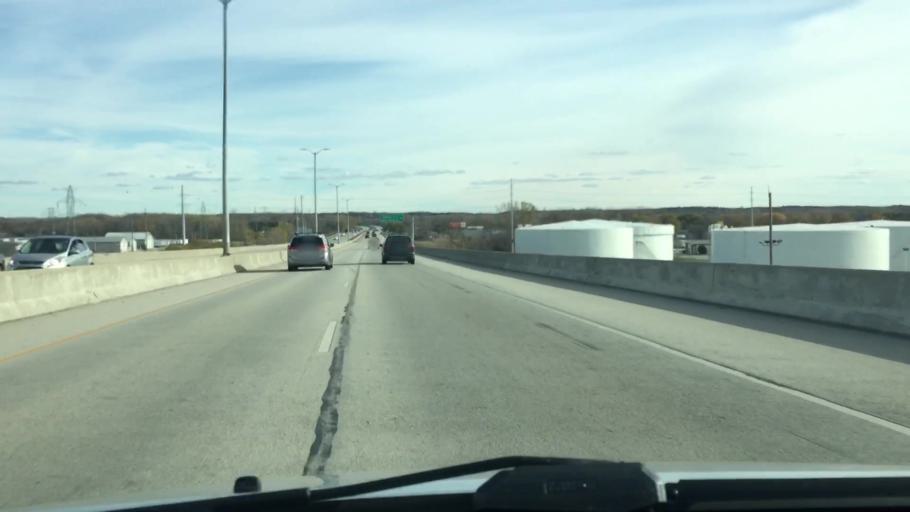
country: US
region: Wisconsin
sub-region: Brown County
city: Green Bay
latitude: 44.5297
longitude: -87.9965
